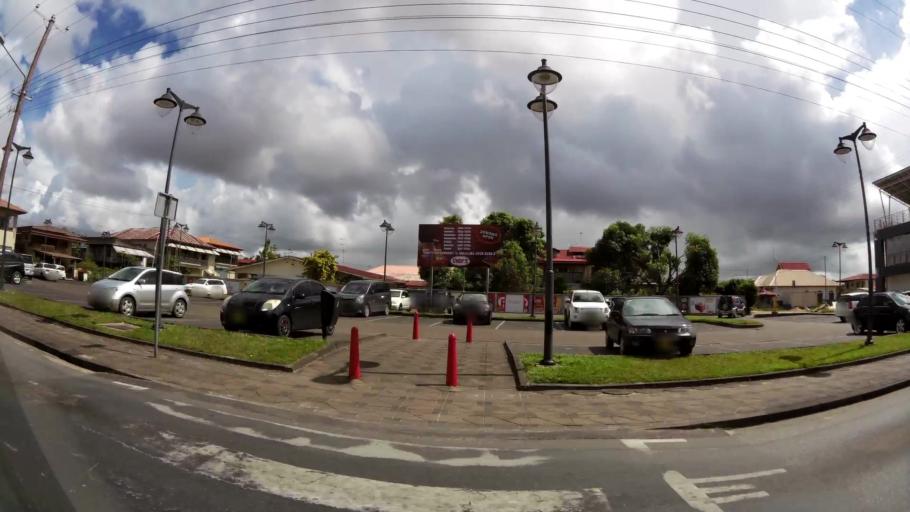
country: SR
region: Paramaribo
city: Paramaribo
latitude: 5.8321
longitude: -55.1901
